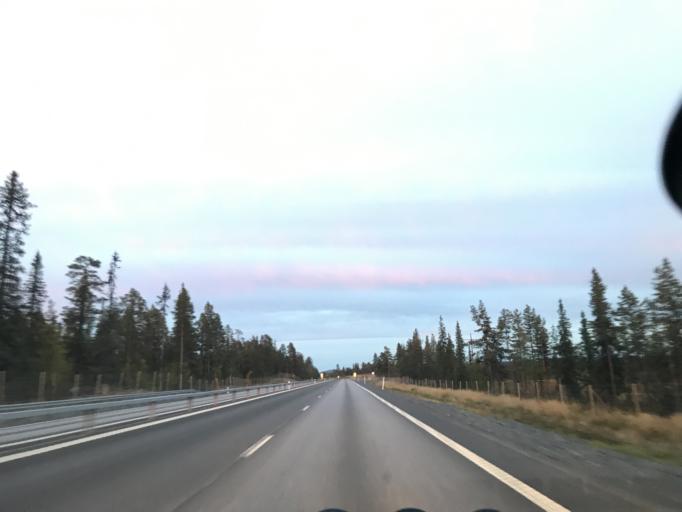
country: SE
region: Norrbotten
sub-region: Gallivare Kommun
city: Malmberget
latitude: 67.6752
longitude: 20.8998
